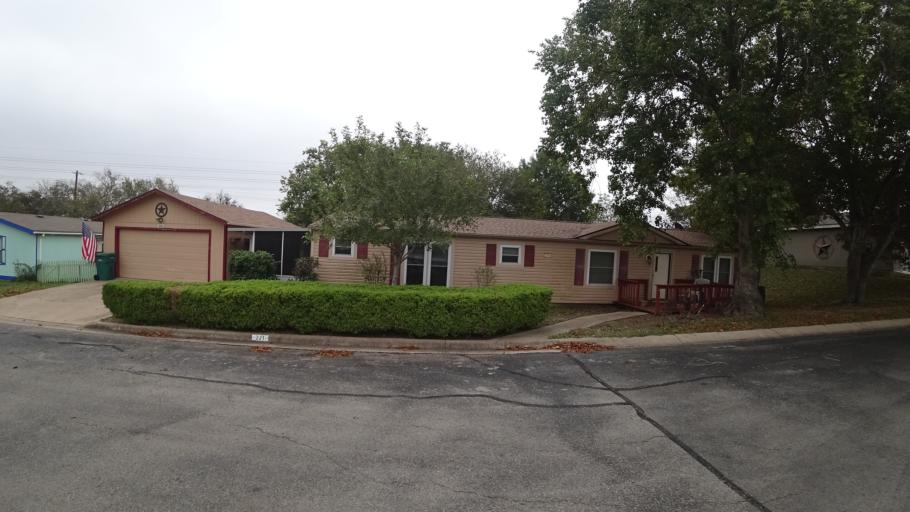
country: US
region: Texas
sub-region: Travis County
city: Pflugerville
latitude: 30.3922
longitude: -97.6395
